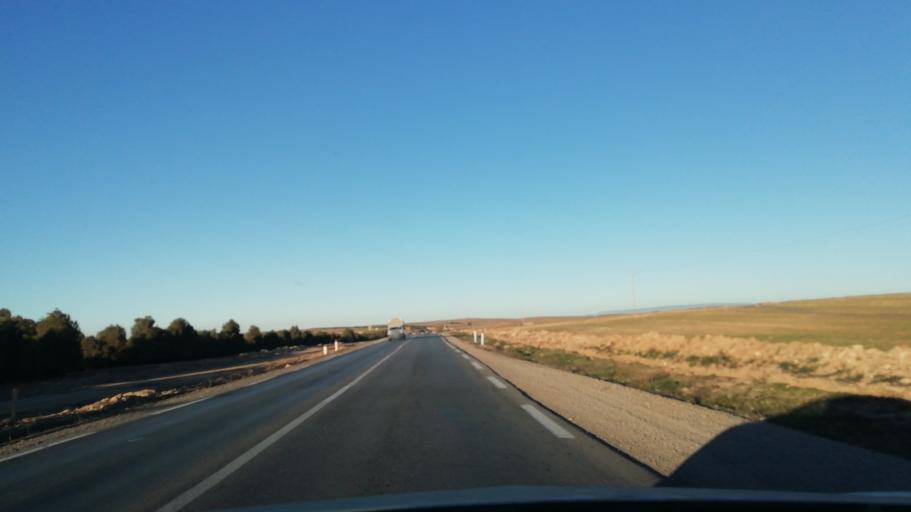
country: DZ
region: Saida
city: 'Ain el Hadjar
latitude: 34.5667
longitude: 0.1221
